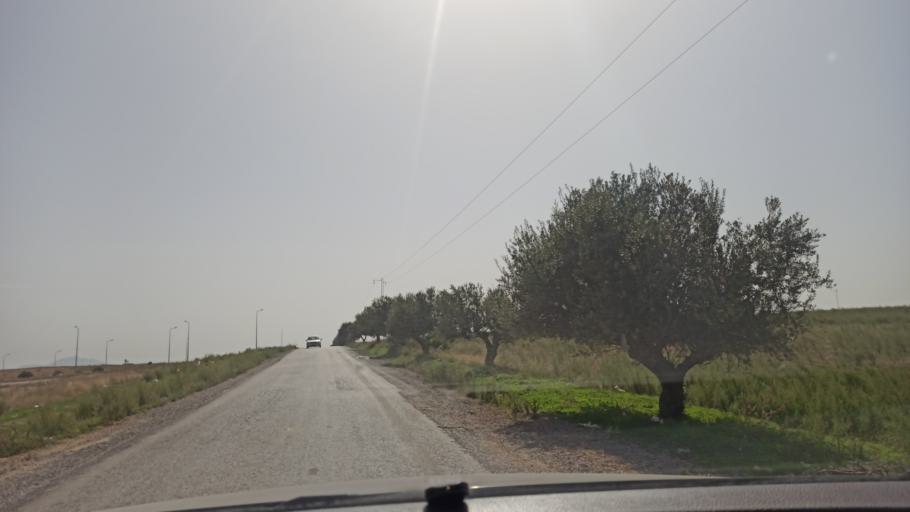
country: TN
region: Manouba
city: Manouba
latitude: 36.7370
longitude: 10.0836
